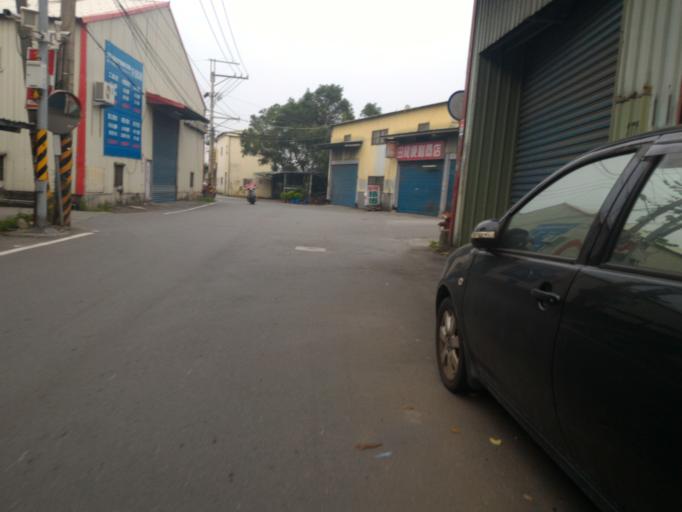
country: TW
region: Taipei
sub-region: Taipei
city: Banqiao
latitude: 24.9541
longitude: 121.4052
